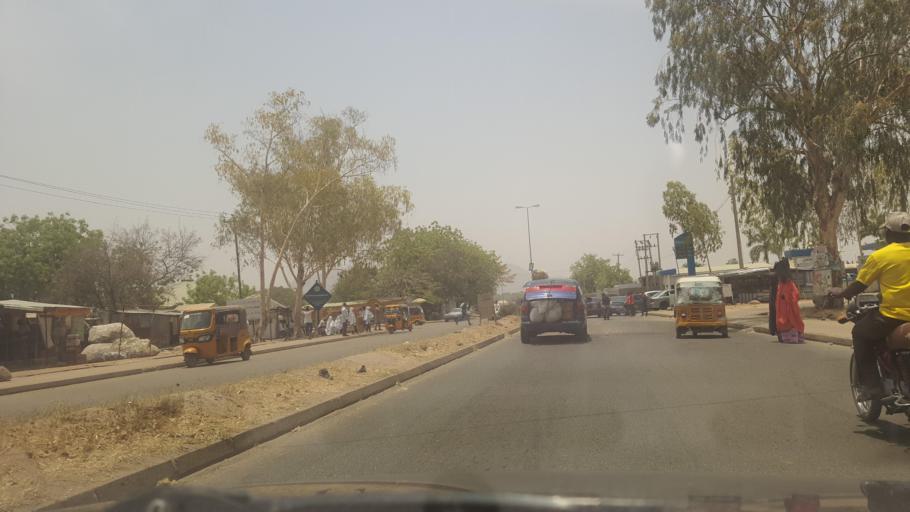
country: NG
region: Bauchi
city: Bauchi
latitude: 10.2940
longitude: 9.8042
